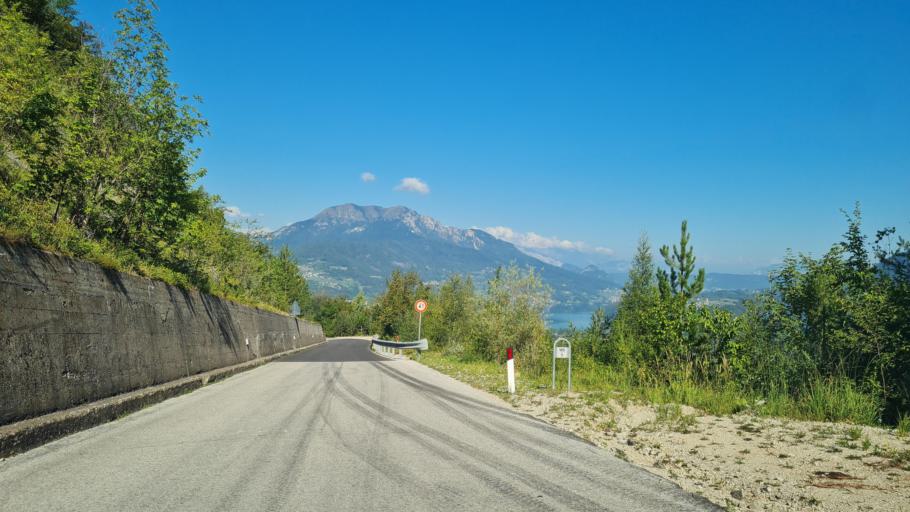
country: IT
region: Trentino-Alto Adige
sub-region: Provincia di Trento
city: Levico Terme
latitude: 45.9805
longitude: 11.2987
